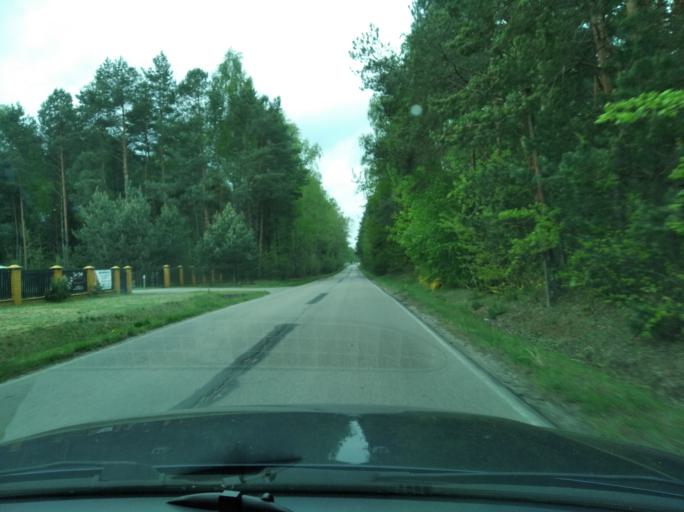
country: PL
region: Subcarpathian Voivodeship
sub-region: Powiat kolbuszowski
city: Kolbuszowa
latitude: 50.1948
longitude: 21.7699
